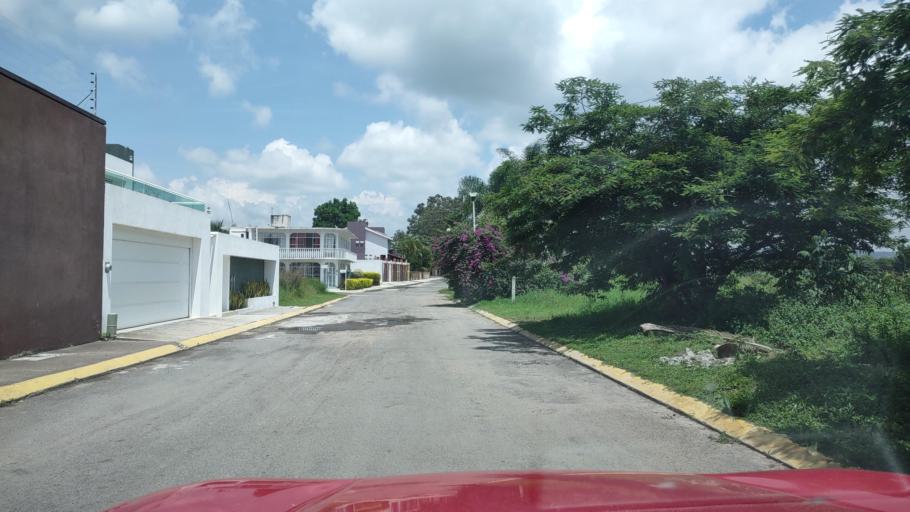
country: MX
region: Veracruz
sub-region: Emiliano Zapata
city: Dos Rios
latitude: 19.4645
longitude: -96.7890
